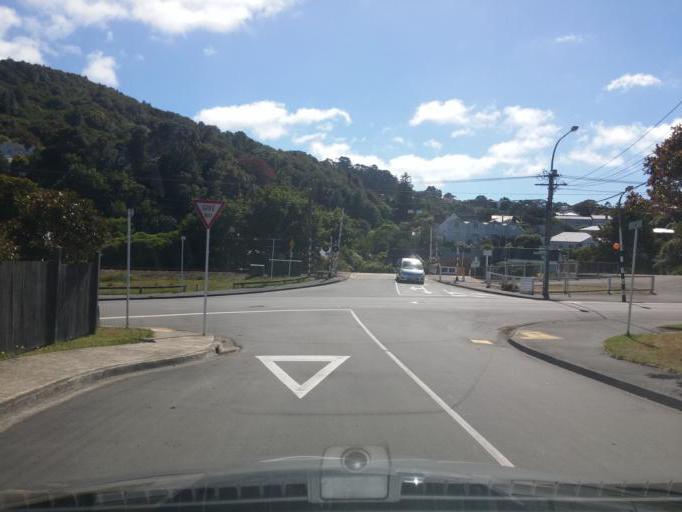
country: NZ
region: Wellington
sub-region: Wellington City
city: Kelburn
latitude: -41.2470
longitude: 174.7835
